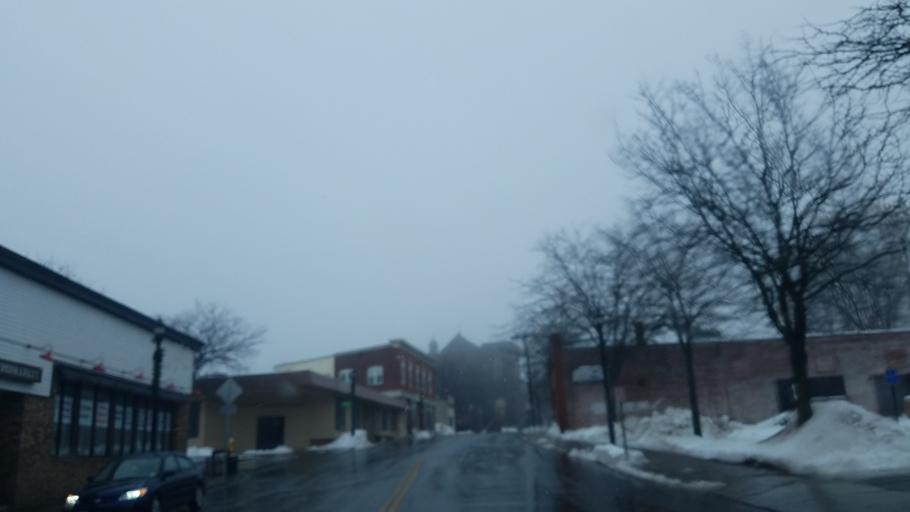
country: US
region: Connecticut
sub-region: Hartford County
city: Thompsonville
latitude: 41.9981
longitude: -72.6002
